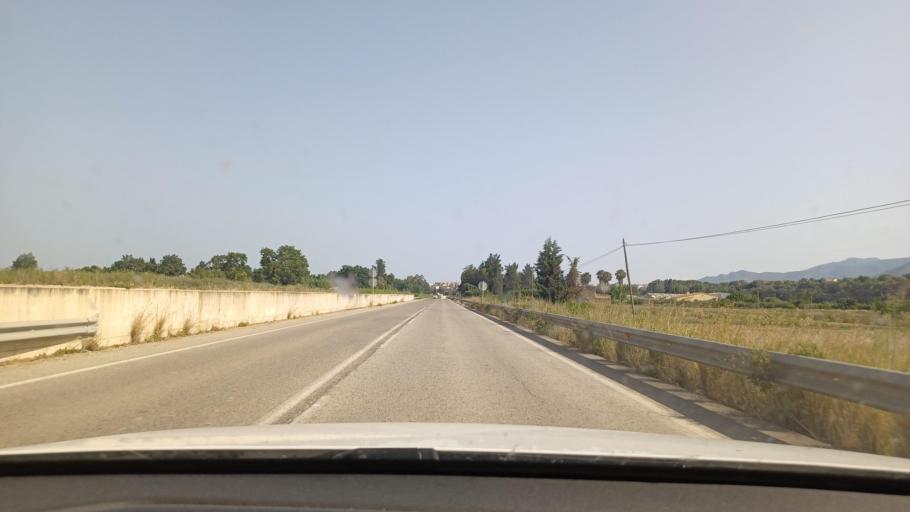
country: ES
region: Catalonia
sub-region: Provincia de Tarragona
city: Amposta
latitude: 40.7252
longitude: 0.5721
